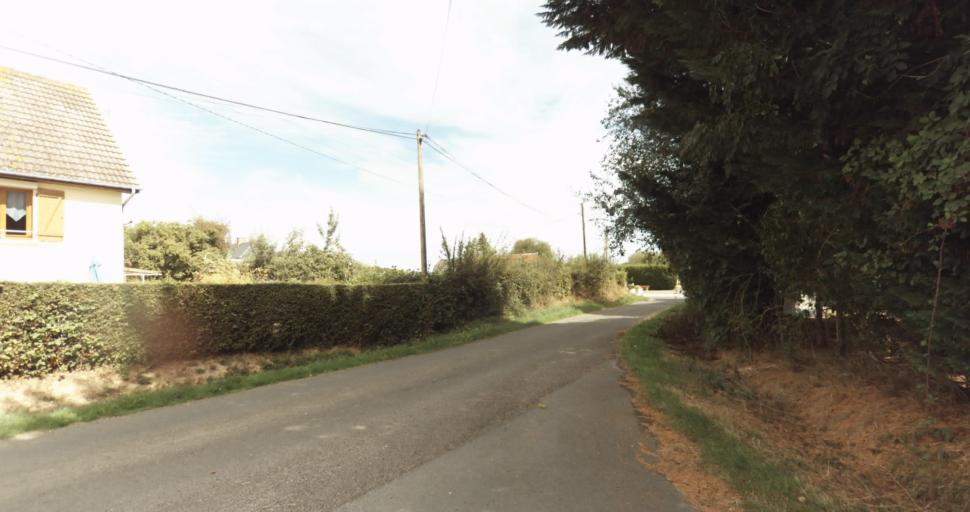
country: FR
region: Lower Normandy
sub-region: Departement du Calvados
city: Orbec
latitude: 48.9246
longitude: 0.3775
